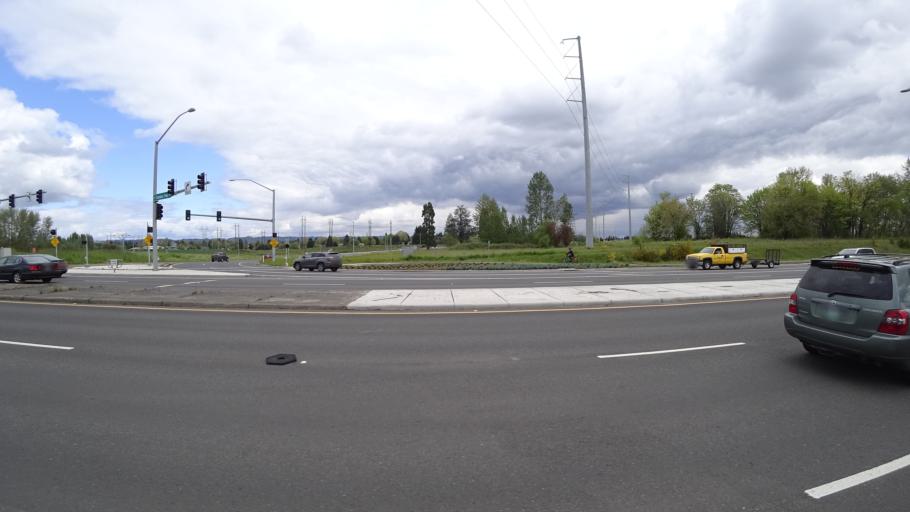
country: US
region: Oregon
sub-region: Washington County
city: Rockcreek
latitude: 45.5529
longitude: -122.9007
